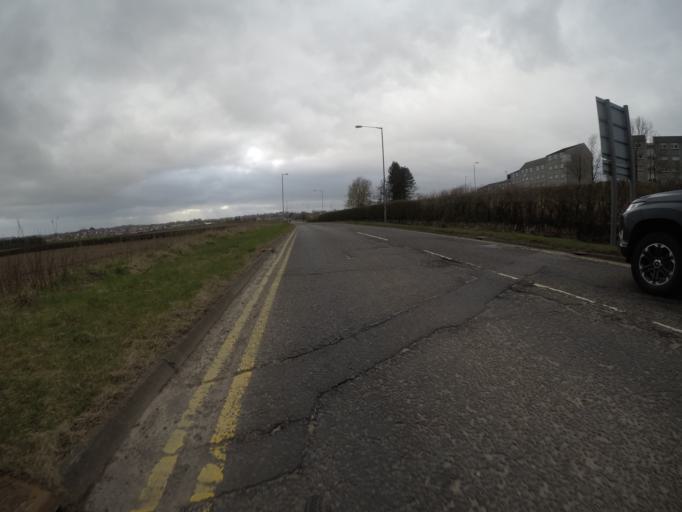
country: GB
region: Scotland
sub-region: East Ayrshire
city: Crosshouse
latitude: 55.6116
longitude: -4.5341
